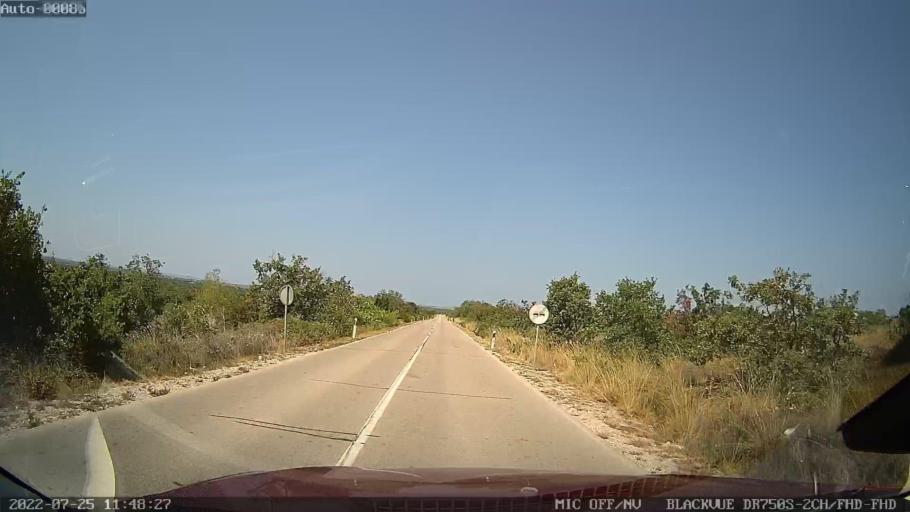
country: HR
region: Zadarska
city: Razanac
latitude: 44.2333
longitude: 15.2983
